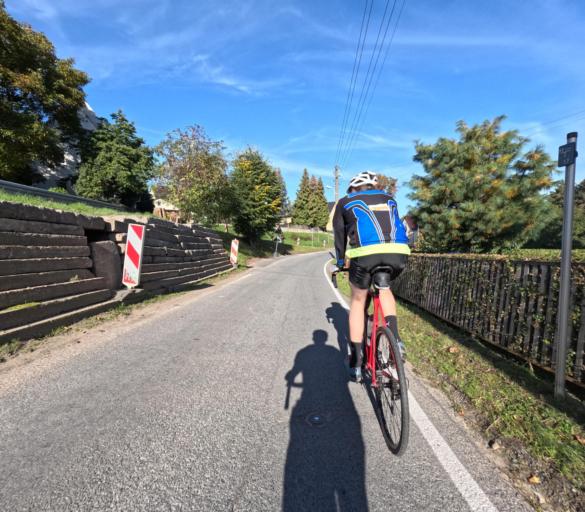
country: DE
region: Saxony
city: Ottendorf-Okrilla
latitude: 51.1362
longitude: 13.8414
